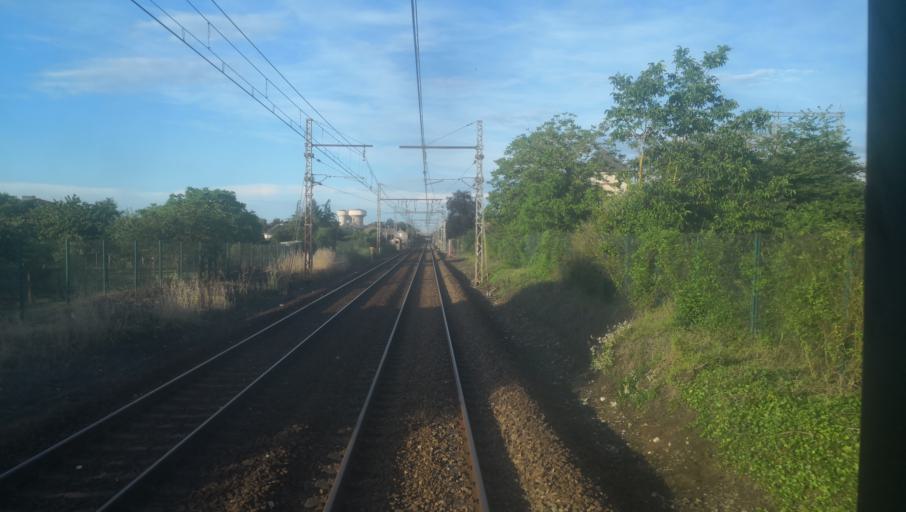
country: FR
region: Centre
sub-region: Departement de l'Indre
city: Chateauroux
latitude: 46.8000
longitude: 1.6766
